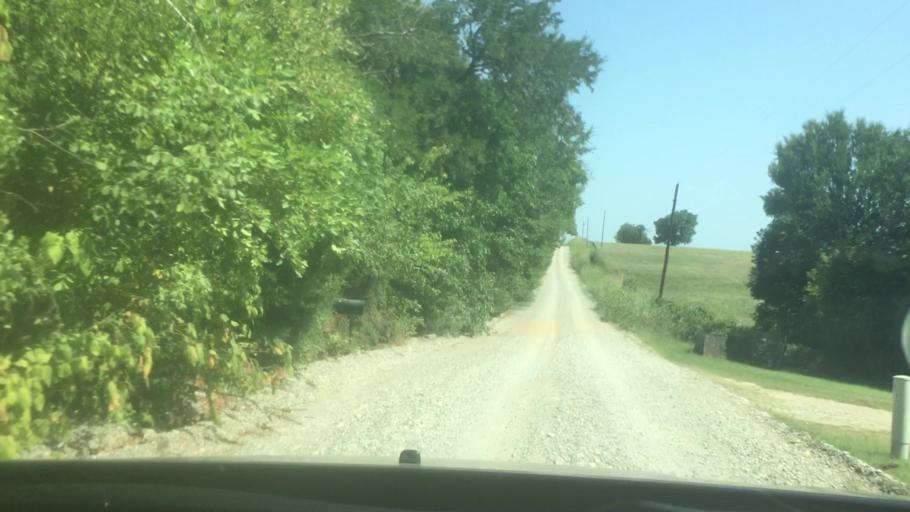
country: US
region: Oklahoma
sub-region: Bryan County
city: Durant
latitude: 34.1356
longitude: -96.4077
